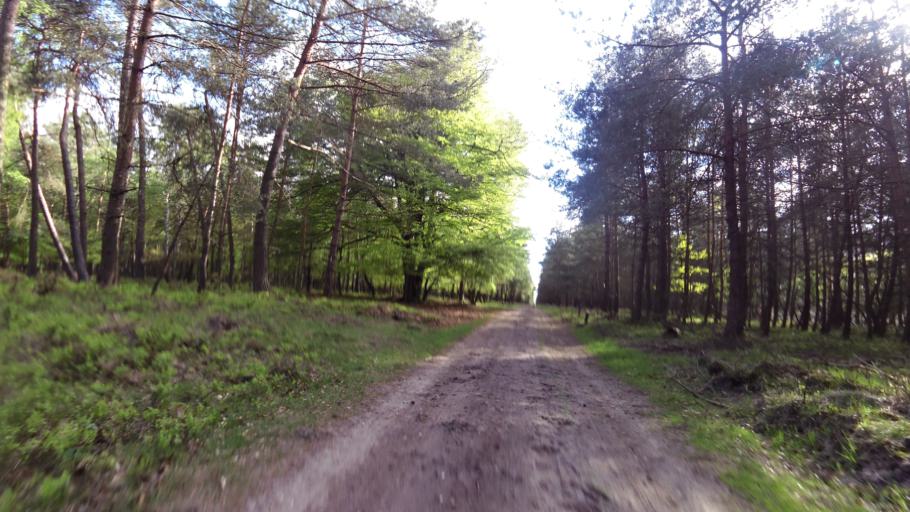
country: NL
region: Gelderland
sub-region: Gemeente Rozendaal
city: Rozendaal
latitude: 52.0721
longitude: 5.9546
